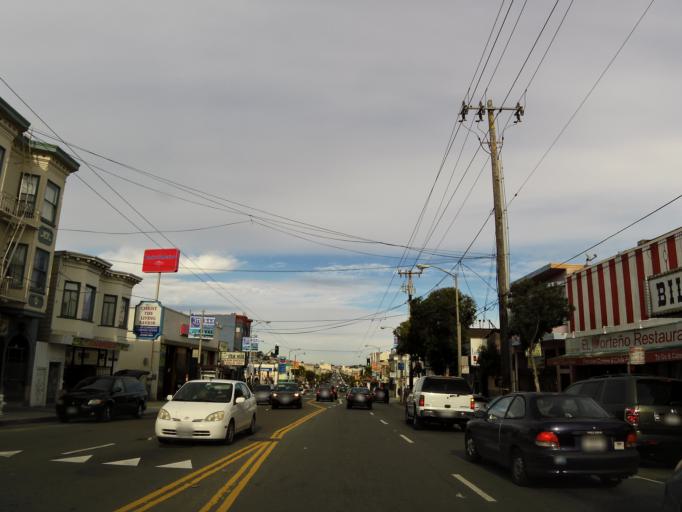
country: US
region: California
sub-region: San Mateo County
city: Daly City
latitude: 37.7158
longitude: -122.4416
